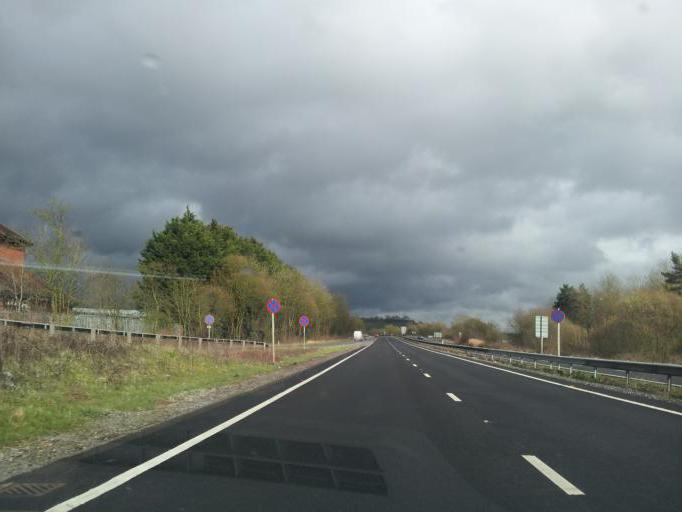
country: GB
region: England
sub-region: Somerset
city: Wincanton
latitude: 51.0485
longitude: -2.4166
